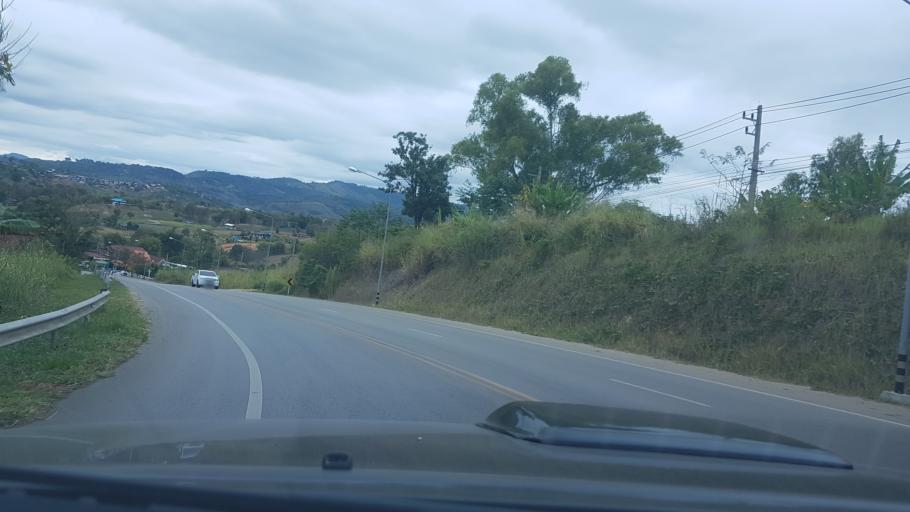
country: TH
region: Phetchabun
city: Khao Kho
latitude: 16.5587
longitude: 101.0254
